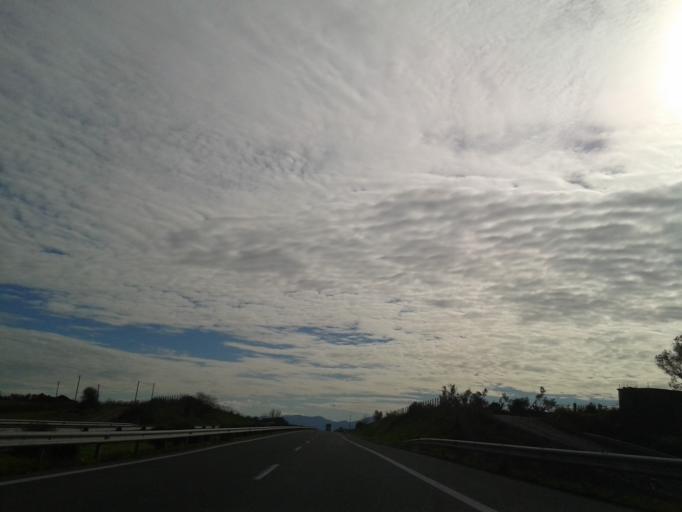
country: GR
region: West Greece
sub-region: Nomos Aitolias kai Akarnanias
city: Fitiai
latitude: 38.6731
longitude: 21.2268
